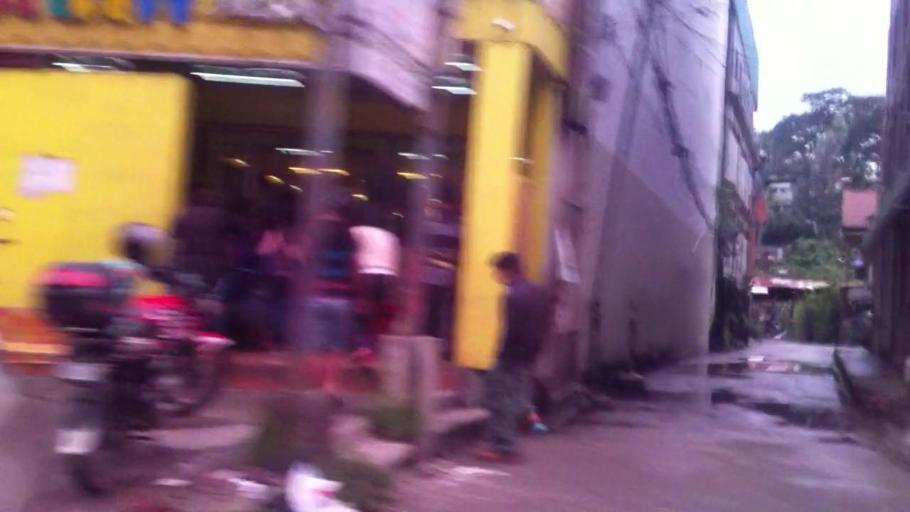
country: PH
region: Cordillera
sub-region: Province of Benguet
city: La Trinidad
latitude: 16.4430
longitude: 120.5923
